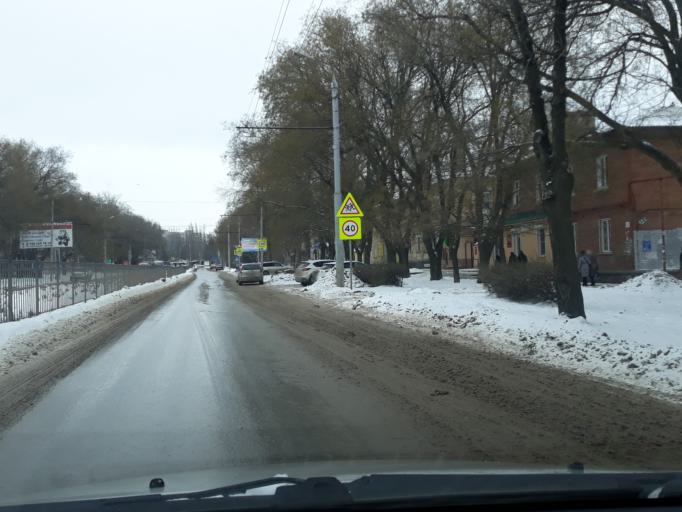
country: RU
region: Rostov
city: Taganrog
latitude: 47.2585
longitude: 38.9180
